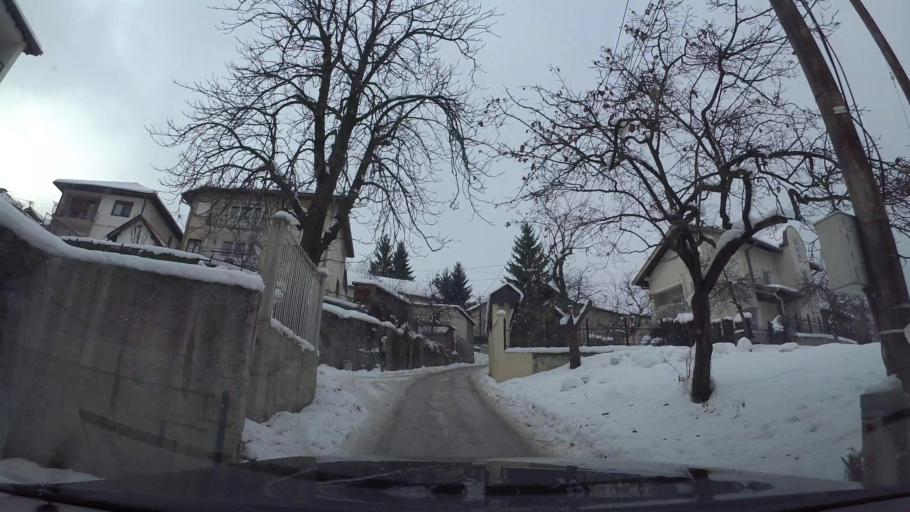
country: BA
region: Federation of Bosnia and Herzegovina
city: Kobilja Glava
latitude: 43.8696
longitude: 18.3987
